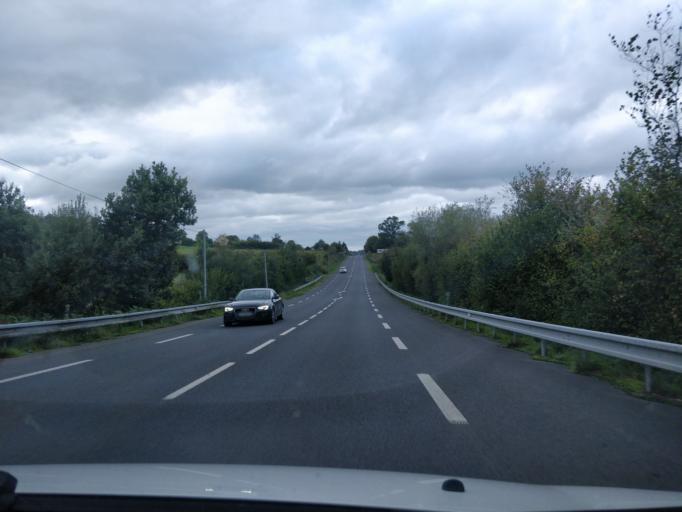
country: FR
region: Lower Normandy
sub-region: Departement de la Manche
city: Villedieu-les-Poeles
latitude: 48.8308
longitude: -1.1681
